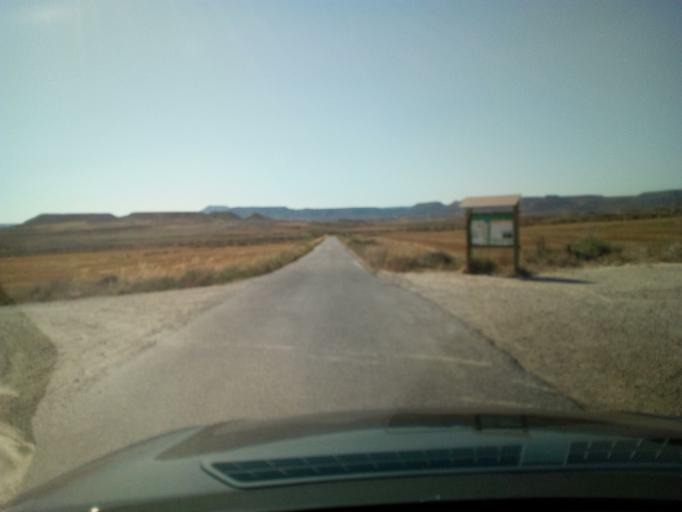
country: ES
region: Navarre
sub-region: Provincia de Navarra
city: Arguedas
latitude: 42.1790
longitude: -1.5228
